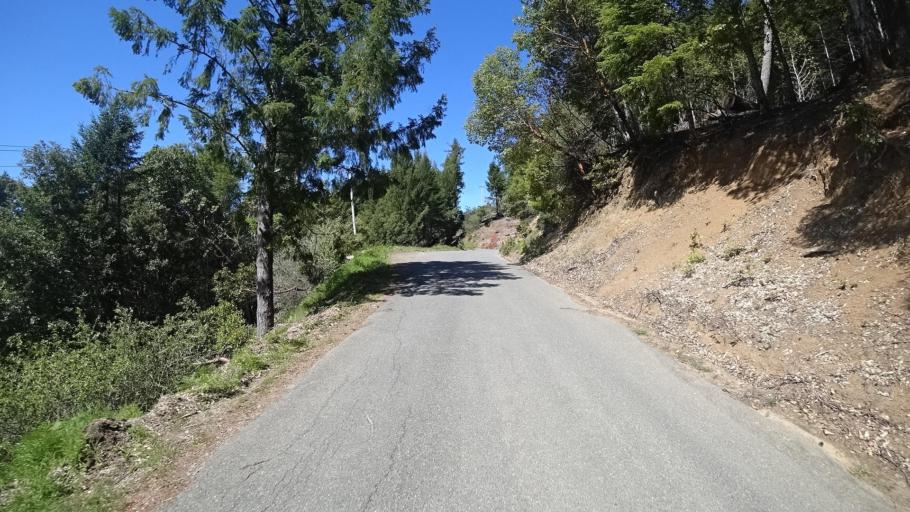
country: US
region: California
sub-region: Humboldt County
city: Redway
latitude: 40.1508
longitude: -124.0272
